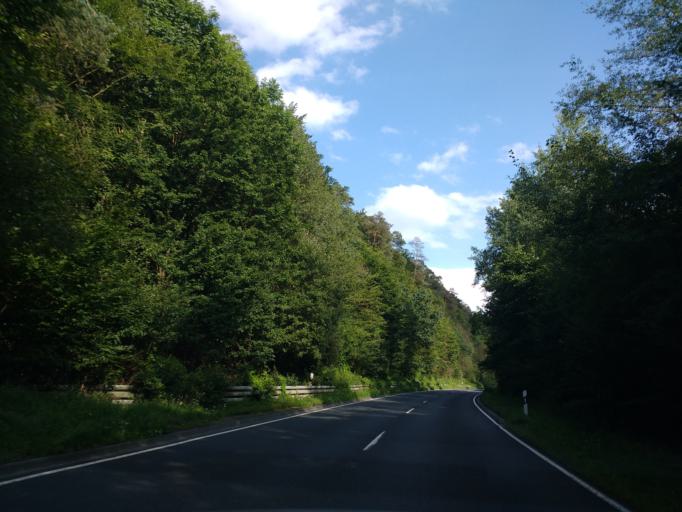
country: DE
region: Hesse
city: Herborn
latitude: 50.7023
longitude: 8.2932
